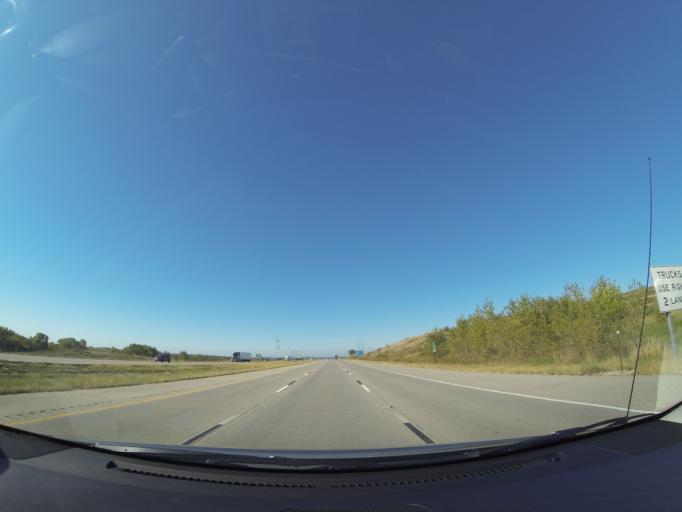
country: US
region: Nebraska
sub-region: Sarpy County
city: Gretna
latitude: 41.0890
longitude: -96.2651
